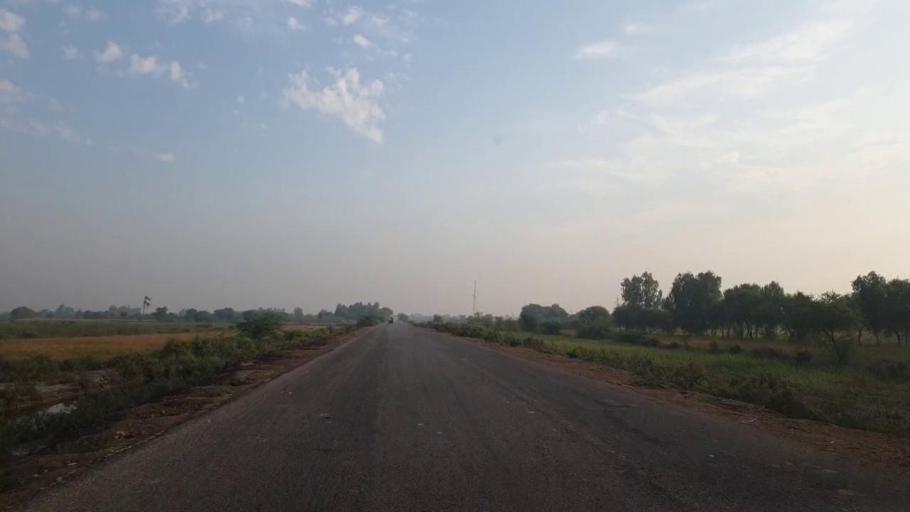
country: PK
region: Sindh
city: Tando Bago
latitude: 24.7014
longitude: 68.9242
